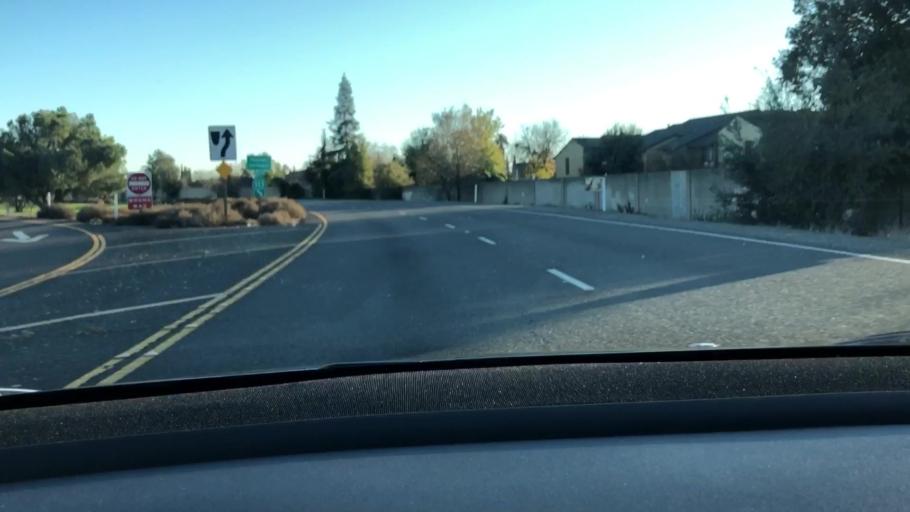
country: US
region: California
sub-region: Yolo County
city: Woodland
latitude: 38.6753
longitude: -121.7530
